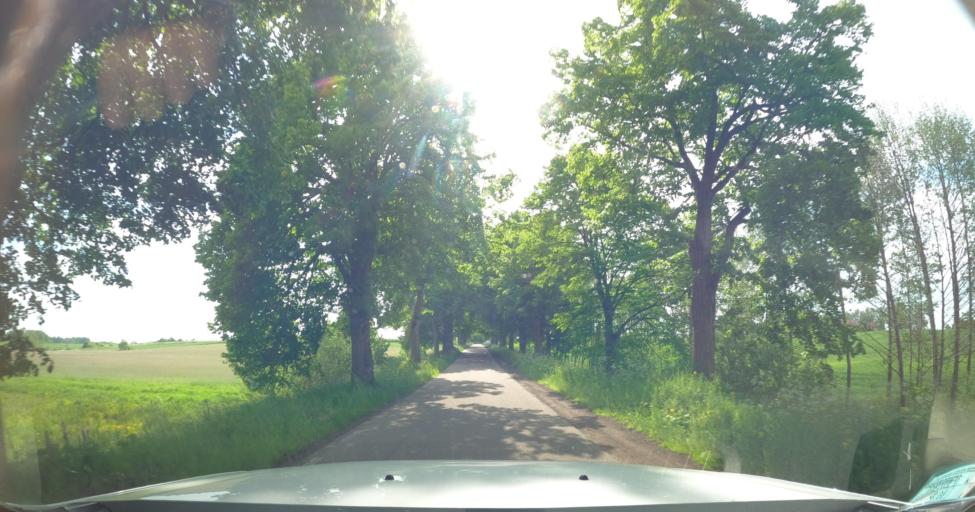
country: PL
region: Warmian-Masurian Voivodeship
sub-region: Powiat lidzbarski
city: Lubomino
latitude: 54.0677
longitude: 20.2155
